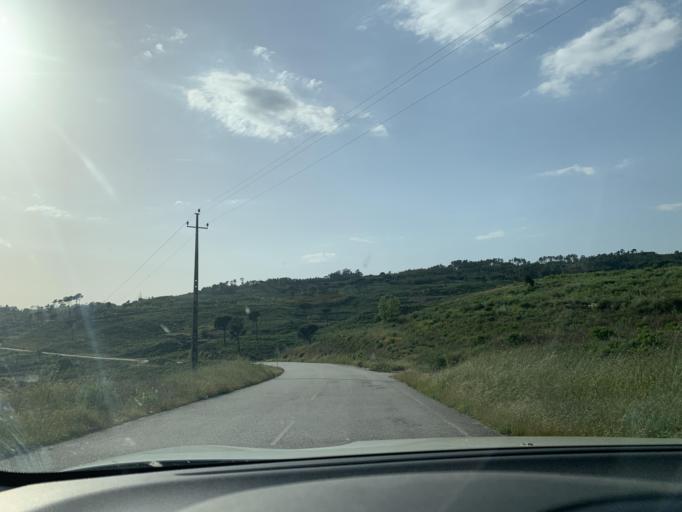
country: PT
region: Viseu
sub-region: Mangualde
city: Mangualde
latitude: 40.5627
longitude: -7.6986
